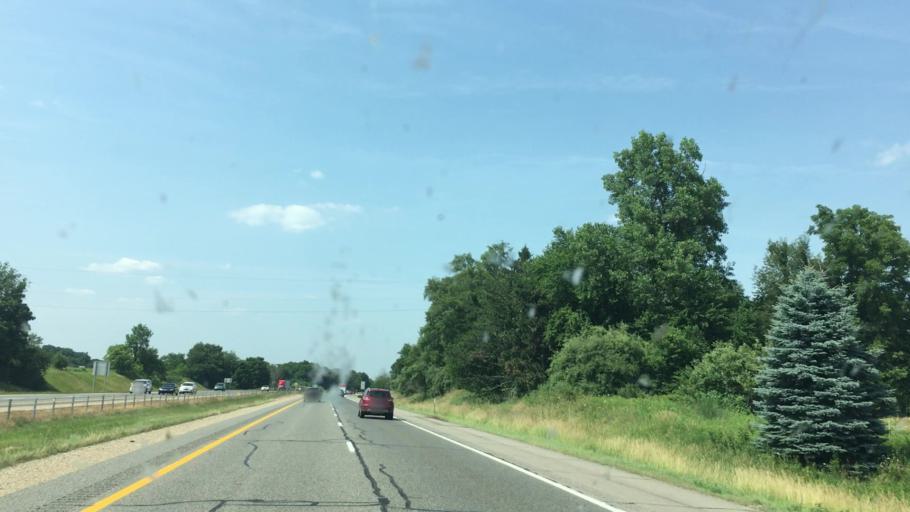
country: US
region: Michigan
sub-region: Allegan County
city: Otsego
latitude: 42.5436
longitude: -85.6612
